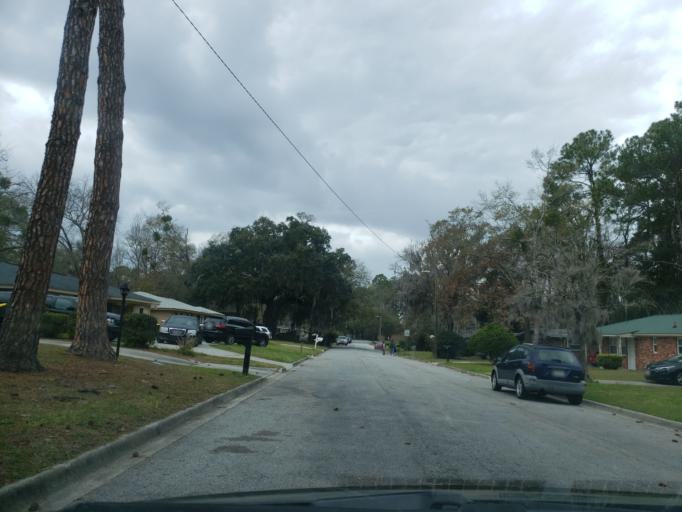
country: US
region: Georgia
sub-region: Chatham County
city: Montgomery
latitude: 31.9943
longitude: -81.1180
